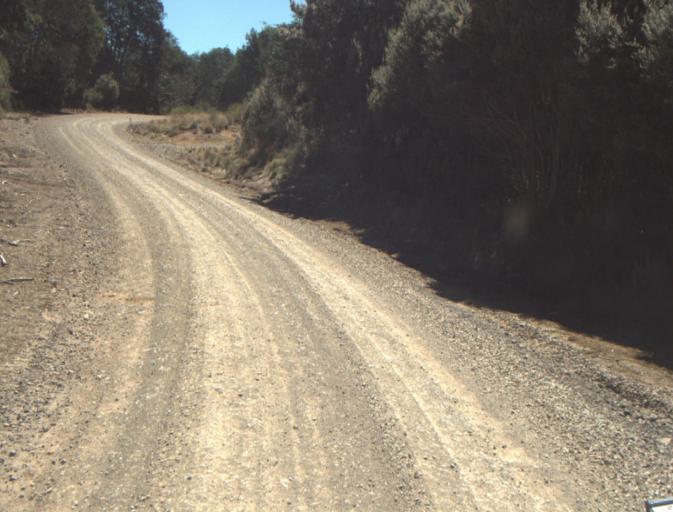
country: AU
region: Tasmania
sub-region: Dorset
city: Scottsdale
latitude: -41.3153
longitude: 147.4649
